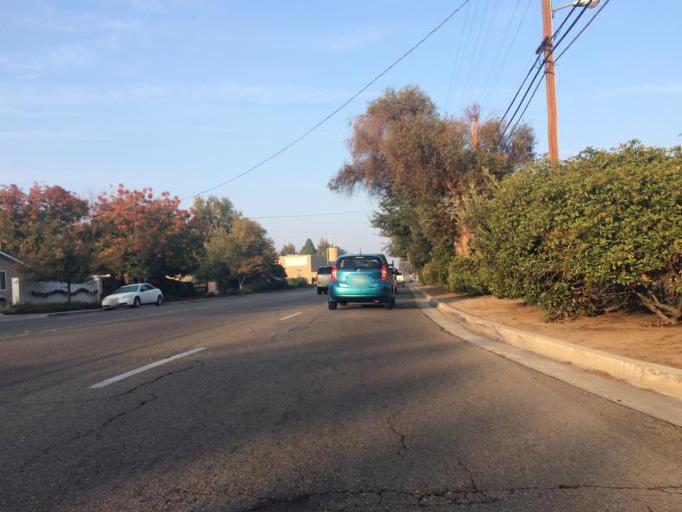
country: US
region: California
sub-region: Fresno County
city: Fresno
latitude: 36.7942
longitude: -119.7654
